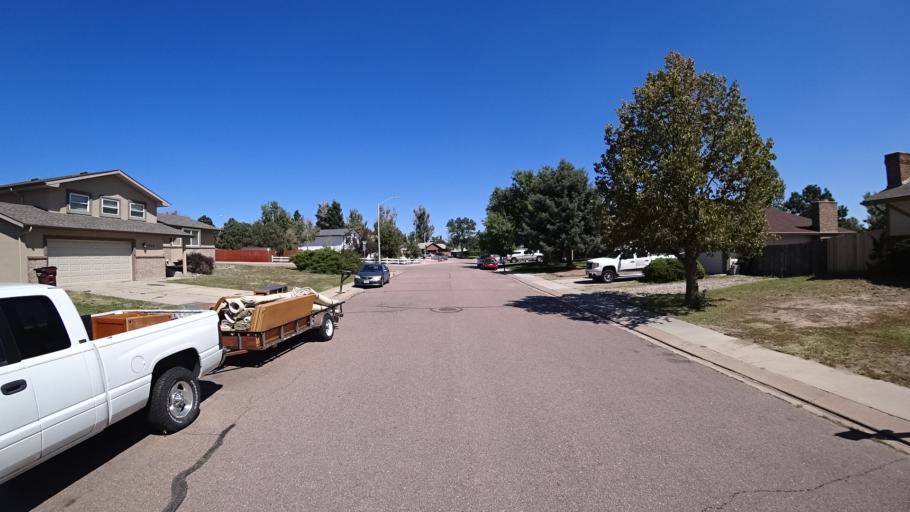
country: US
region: Colorado
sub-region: El Paso County
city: Cimarron Hills
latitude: 38.8698
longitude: -104.7237
